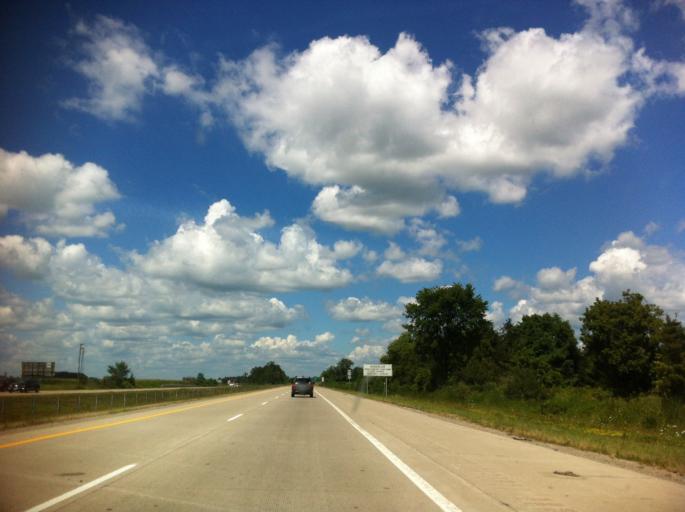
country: US
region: Ohio
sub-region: Lucas County
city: Sylvania
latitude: 41.7748
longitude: -83.6951
